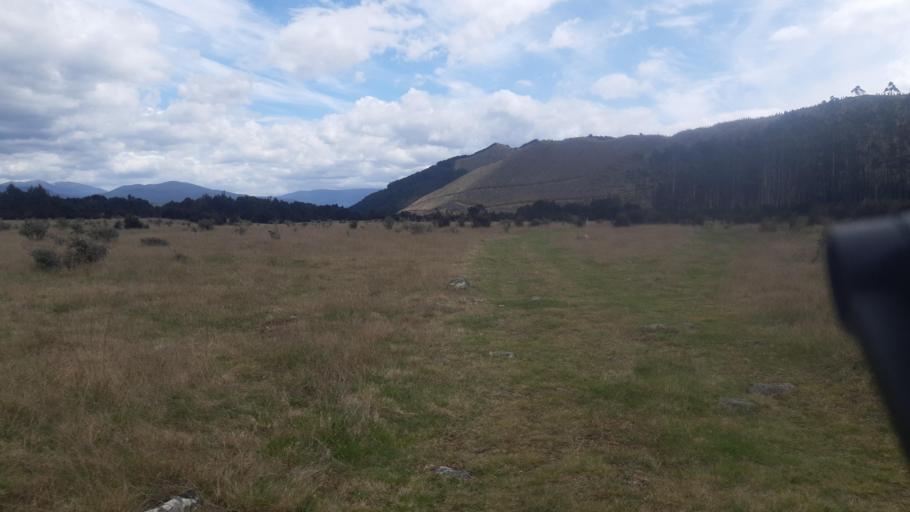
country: NZ
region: Tasman
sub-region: Tasman District
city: Wakefield
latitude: -41.7720
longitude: 172.7999
